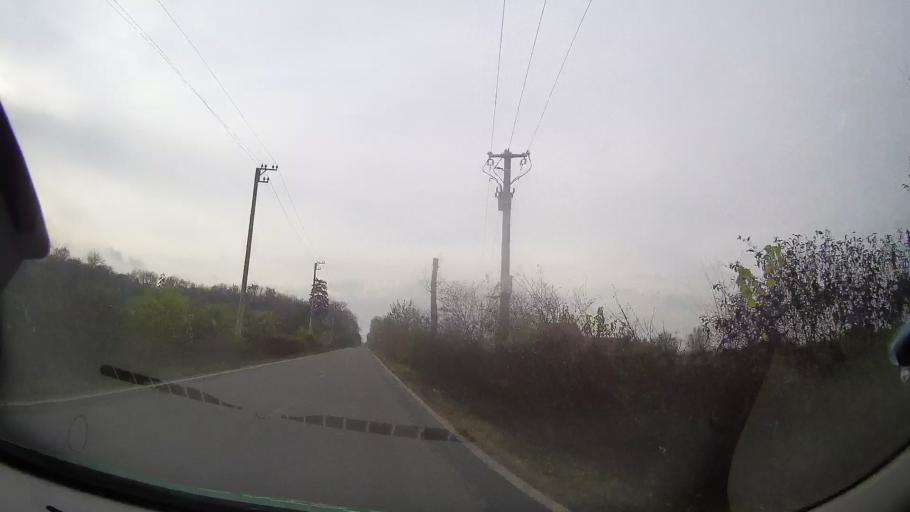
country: RO
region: Prahova
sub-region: Comuna Balta Doamnei
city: Balta Doamnei
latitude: 44.7437
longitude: 26.1417
